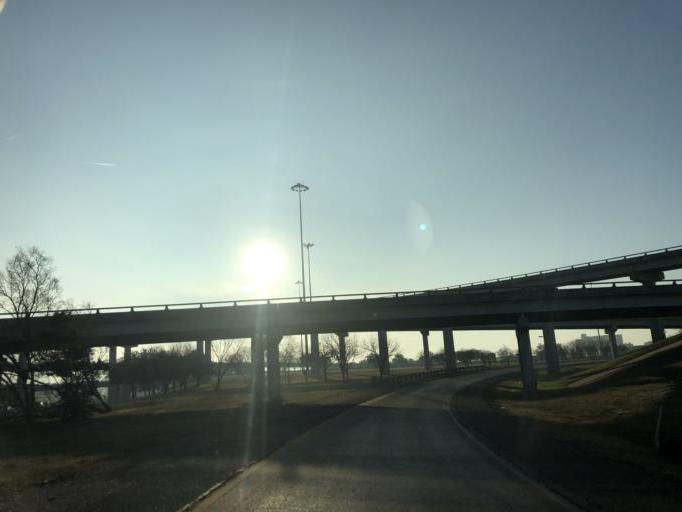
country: US
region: Texas
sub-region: Dallas County
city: Duncanville
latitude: 32.6546
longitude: -96.8799
